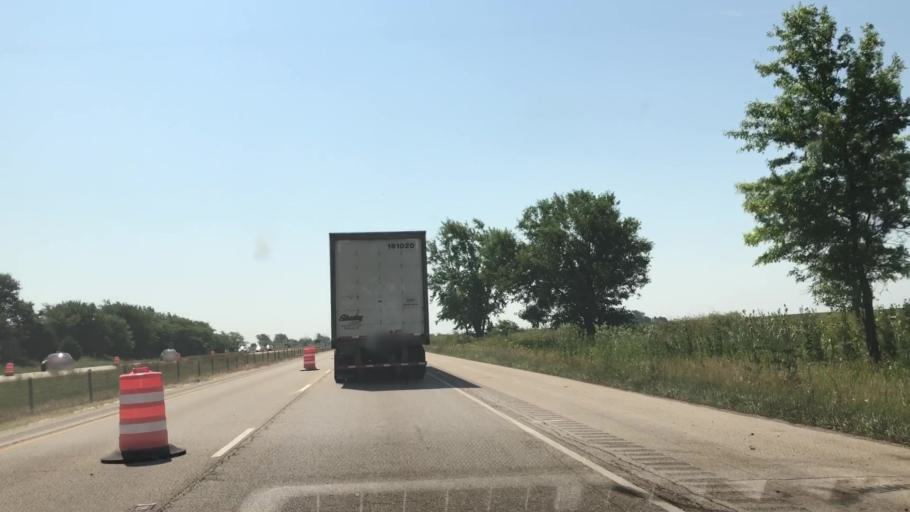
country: US
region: Illinois
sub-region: McLean County
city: Danvers
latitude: 40.5756
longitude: -89.1326
